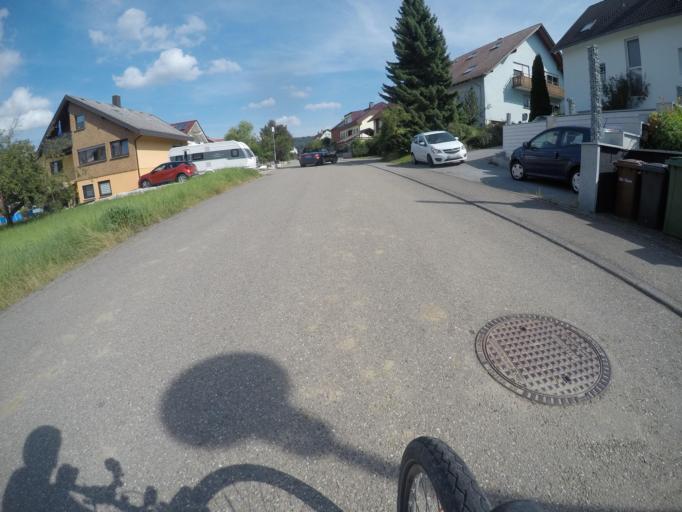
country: DE
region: Baden-Wuerttemberg
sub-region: Karlsruhe Region
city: Olbronn-Durrn
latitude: 48.9830
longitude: 8.7445
